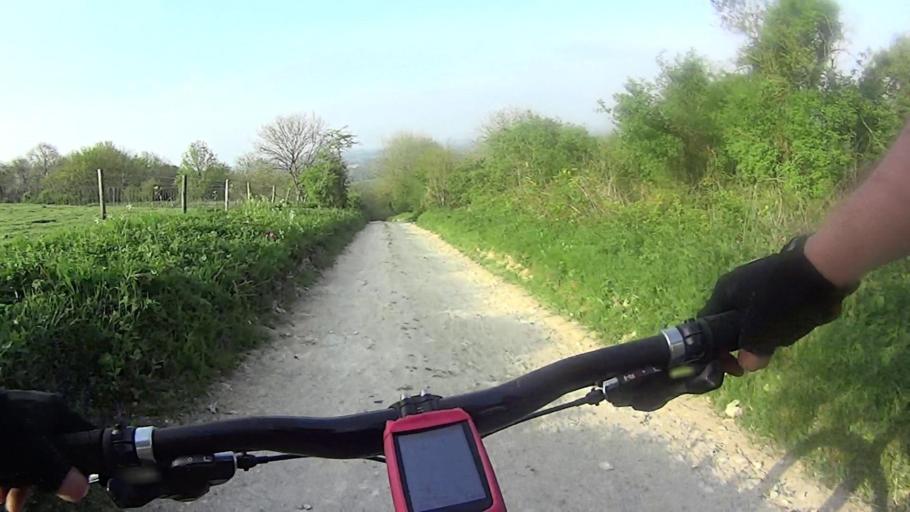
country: GB
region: England
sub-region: West Sussex
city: Walberton
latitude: 50.9081
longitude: -0.5965
